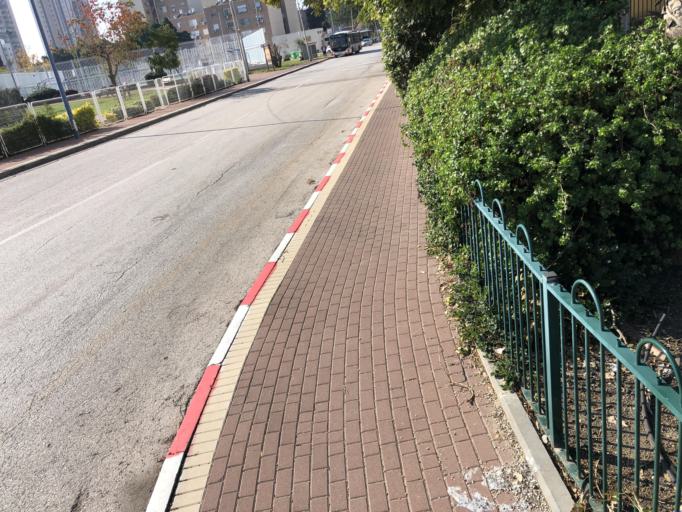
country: IL
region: Northern District
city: `Akko
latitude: 32.9220
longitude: 35.0967
